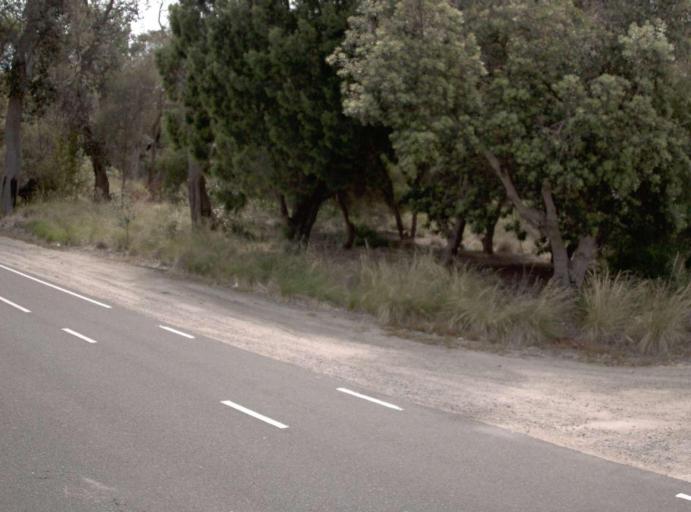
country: AU
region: Victoria
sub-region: Mornington Peninsula
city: Rosebud West
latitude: -38.3624
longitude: 144.8811
